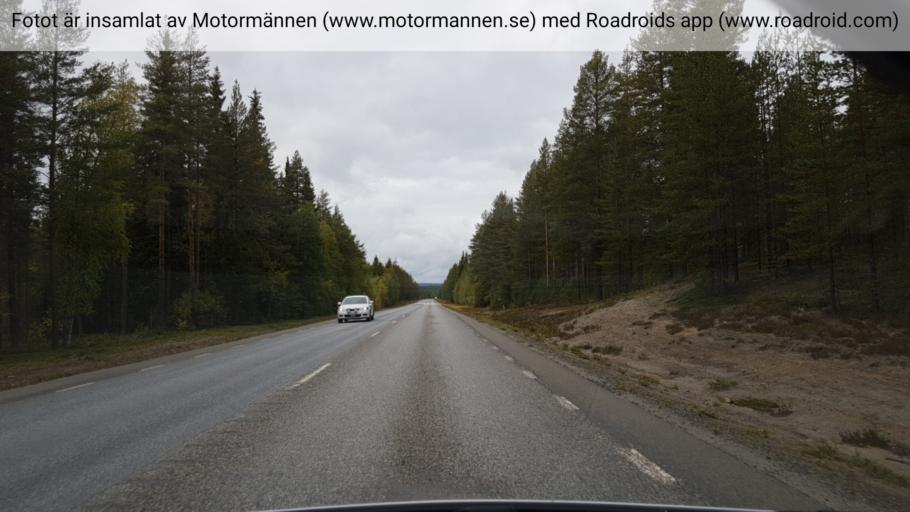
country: SE
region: Vaesterbotten
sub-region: Norsjo Kommun
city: Norsjoe
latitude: 64.9832
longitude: 19.5171
